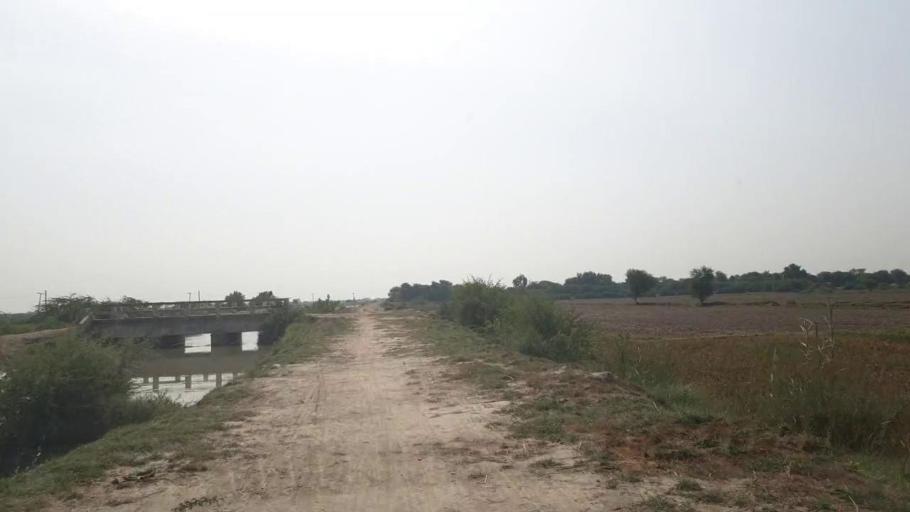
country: PK
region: Sindh
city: Badin
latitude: 24.5542
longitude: 68.8496
